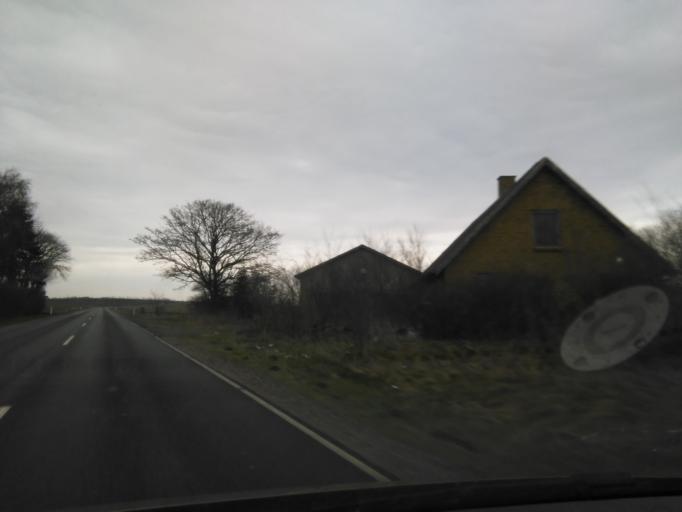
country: DK
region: North Denmark
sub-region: Mariagerfjord Kommune
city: Mariager
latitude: 56.6835
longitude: 9.8962
